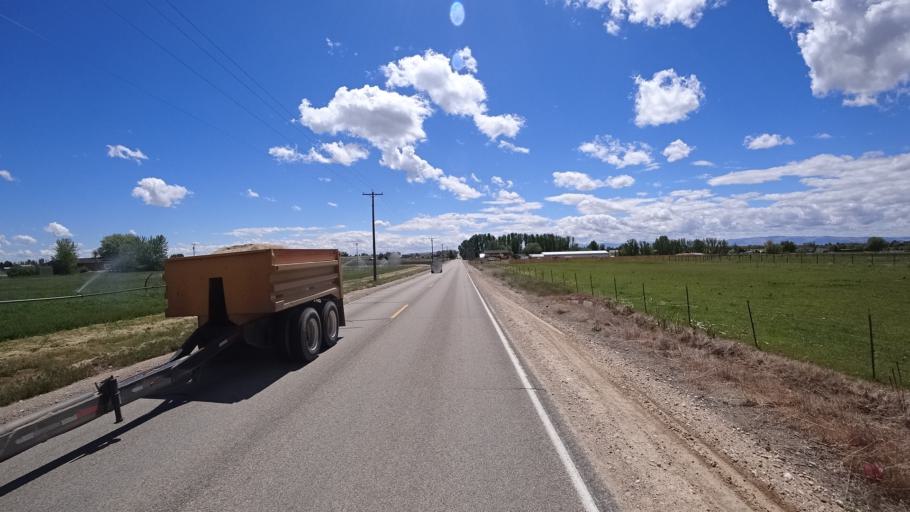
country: US
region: Idaho
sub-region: Ada County
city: Meridian
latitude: 43.5843
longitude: -116.4537
